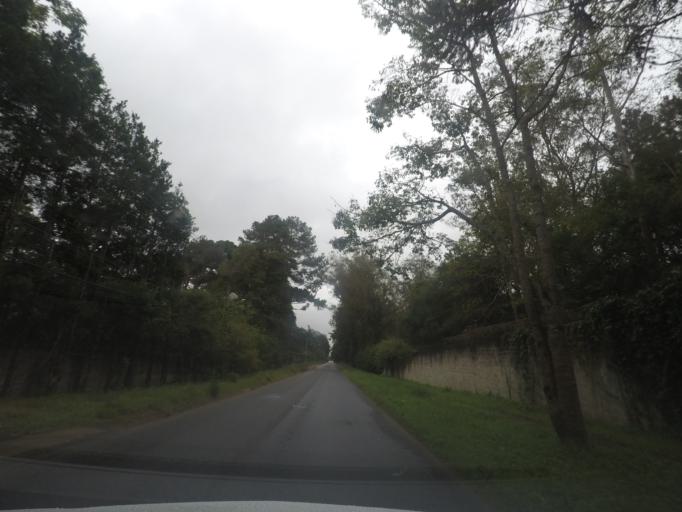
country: BR
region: Parana
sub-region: Pinhais
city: Pinhais
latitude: -25.3896
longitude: -49.1485
